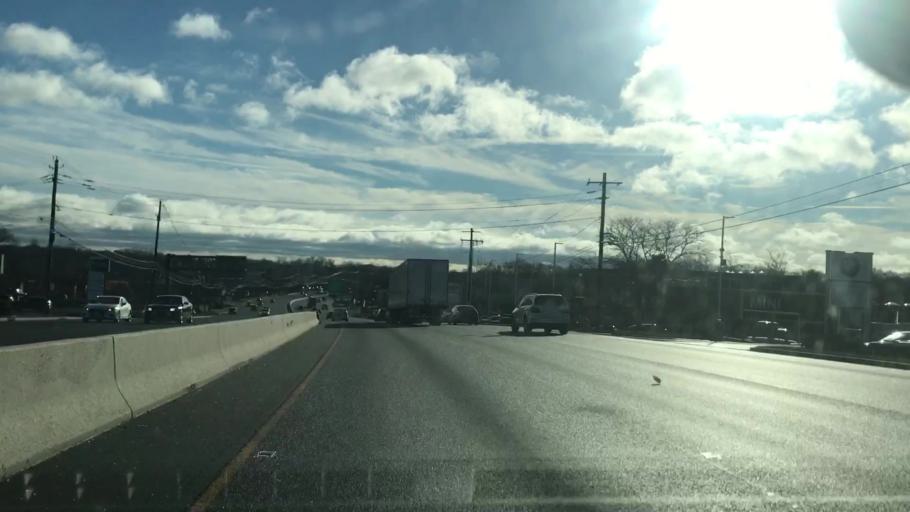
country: US
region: New Jersey
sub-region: Bergen County
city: Ramsey
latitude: 41.0654
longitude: -74.1310
